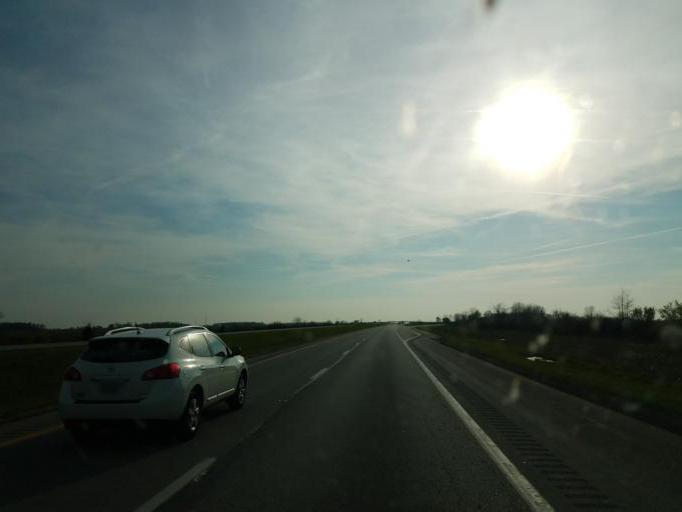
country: US
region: Ohio
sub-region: Clinton County
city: Wilmington
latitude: 39.5346
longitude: -83.7896
